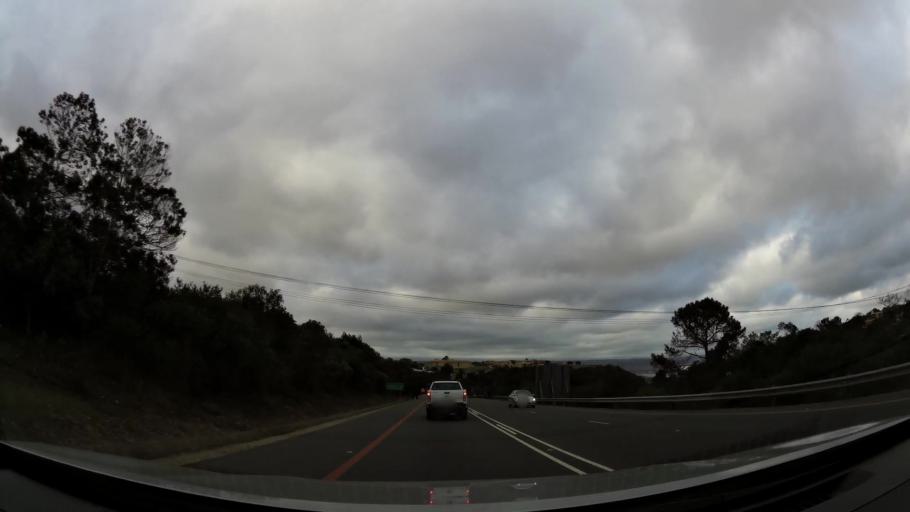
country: ZA
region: Western Cape
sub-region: Eden District Municipality
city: Plettenberg Bay
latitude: -34.0471
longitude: 23.3610
